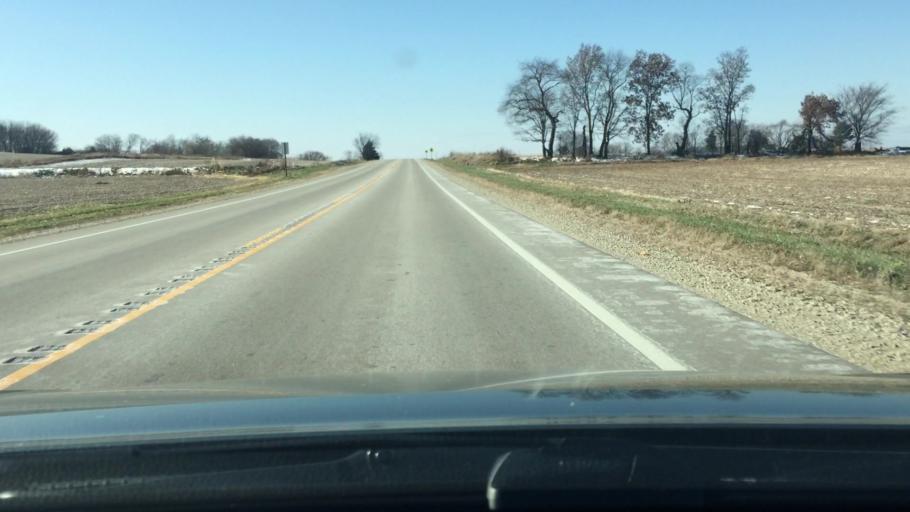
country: US
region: Wisconsin
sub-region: Jefferson County
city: Lake Mills
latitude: 43.0077
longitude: -88.8978
